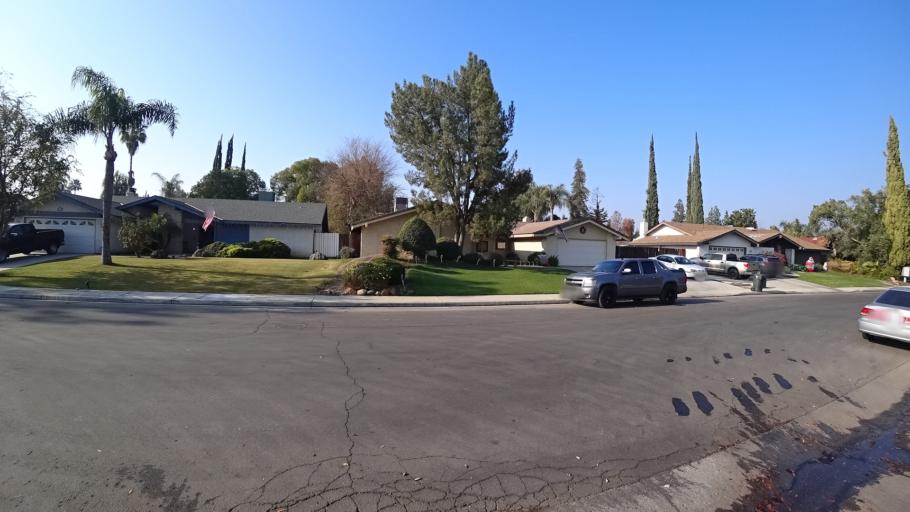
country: US
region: California
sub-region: Kern County
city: Greenacres
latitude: 35.3403
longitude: -119.0824
